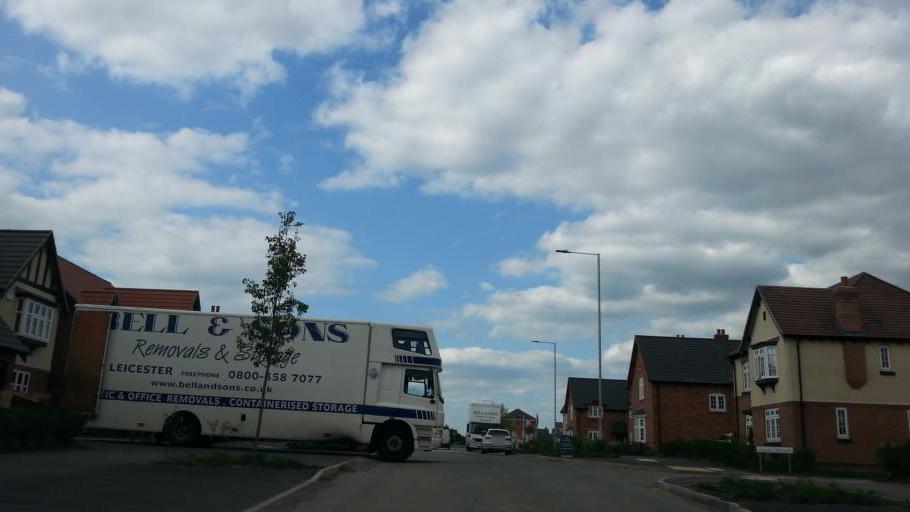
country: GB
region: England
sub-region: Leicestershire
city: Kirby Muxloe
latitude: 52.6111
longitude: -1.2248
